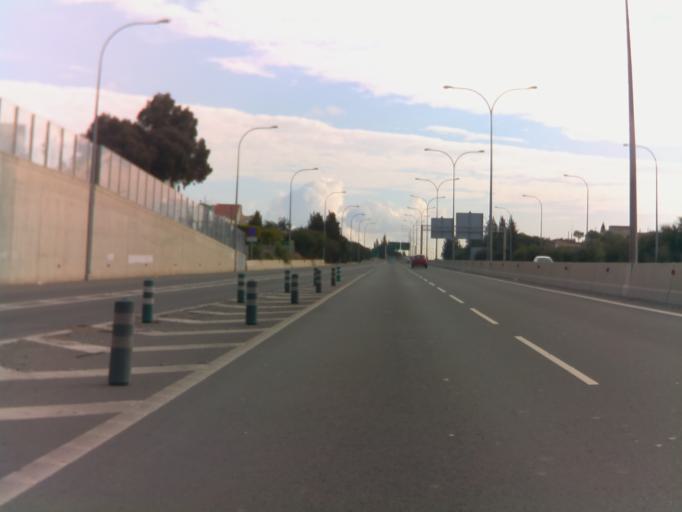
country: CY
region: Limassol
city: Limassol
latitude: 34.7047
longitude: 33.0318
